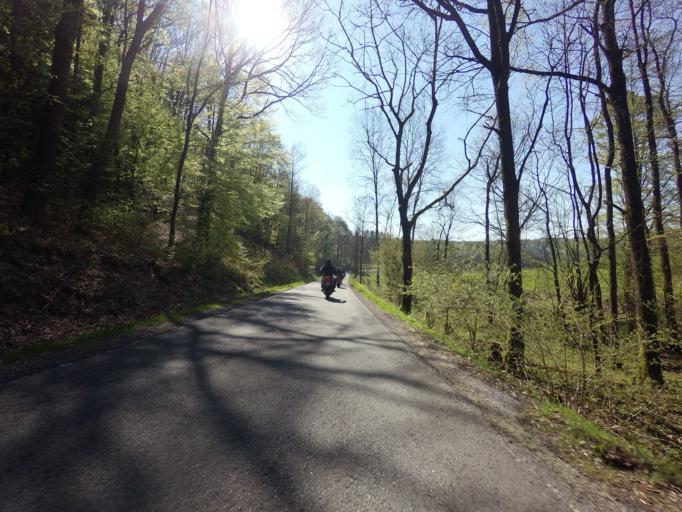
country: DE
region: North Rhine-Westphalia
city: Meinerzhagen
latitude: 51.1171
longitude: 7.7093
